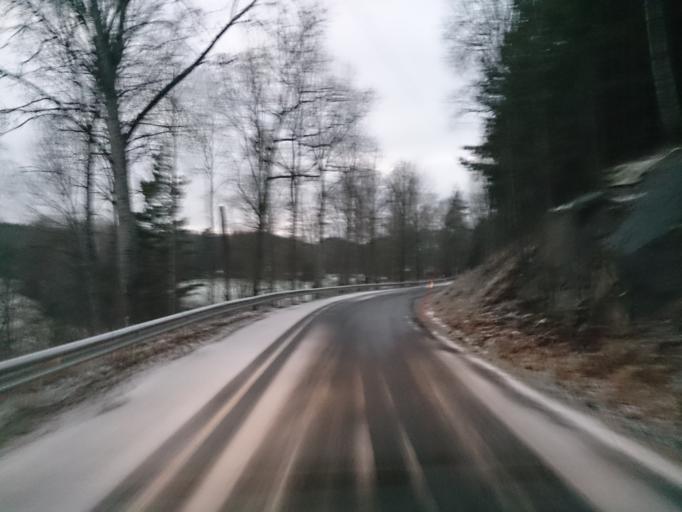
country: SE
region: OEstergoetland
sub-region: Atvidabergs Kommun
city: Atvidaberg
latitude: 58.2794
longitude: 16.1551
